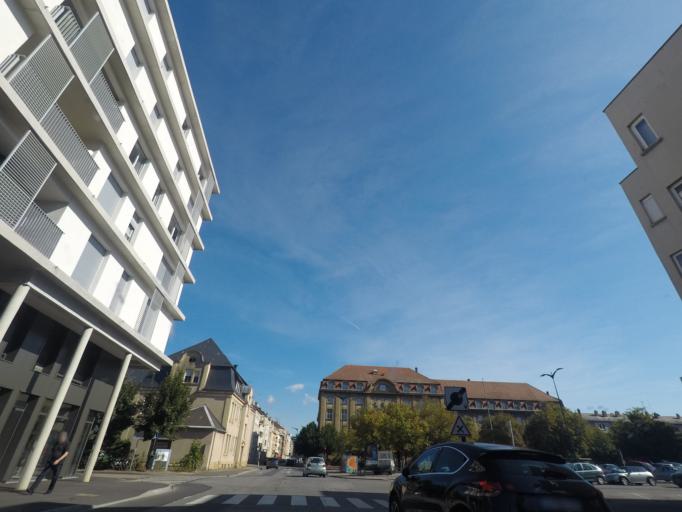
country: FR
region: Lorraine
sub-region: Departement de la Moselle
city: Thionville
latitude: 49.3600
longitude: 6.1665
